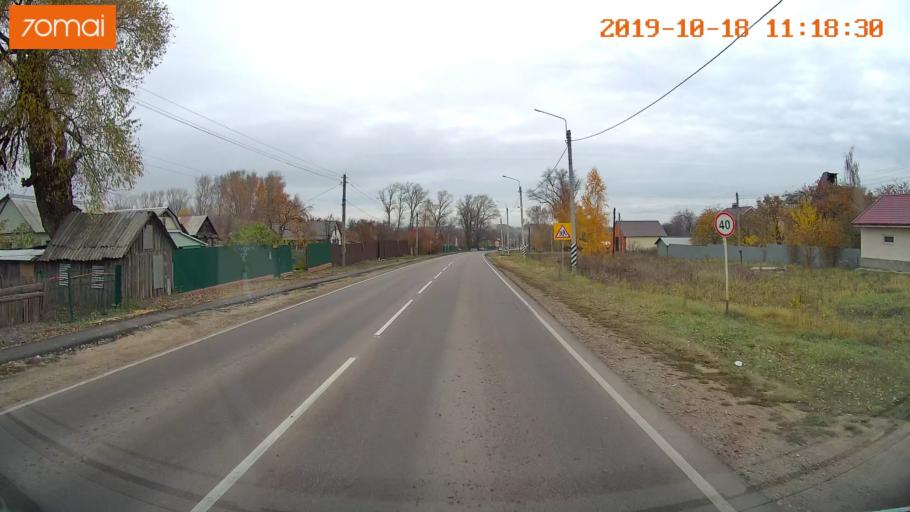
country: RU
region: Tula
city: Kimovsk
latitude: 54.0397
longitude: 38.5504
